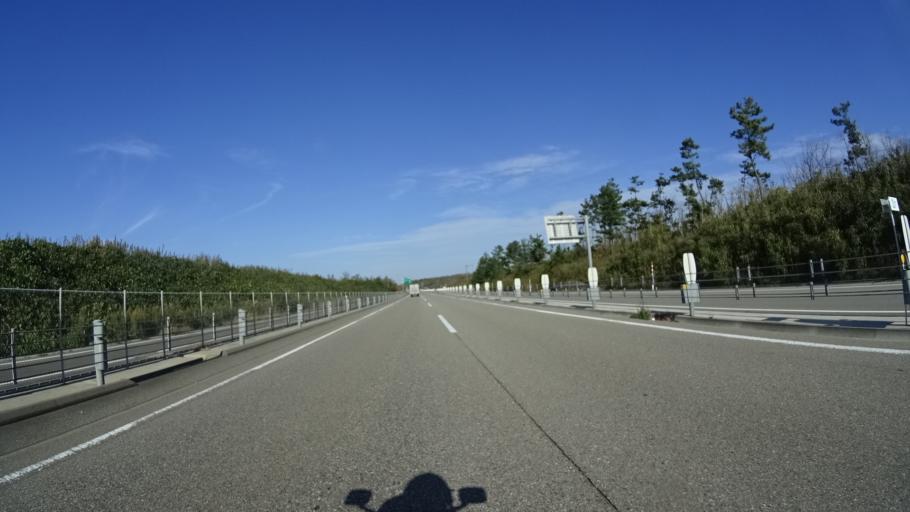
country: JP
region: Ishikawa
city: Kanazawa-shi
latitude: 36.6606
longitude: 136.6422
